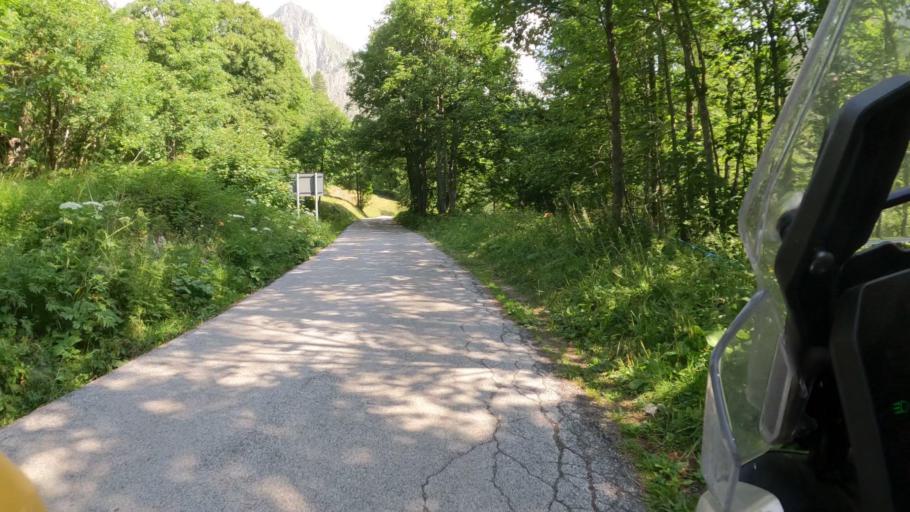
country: IT
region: Piedmont
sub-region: Provincia di Cuneo
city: Canosio
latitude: 44.4280
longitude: 7.0535
